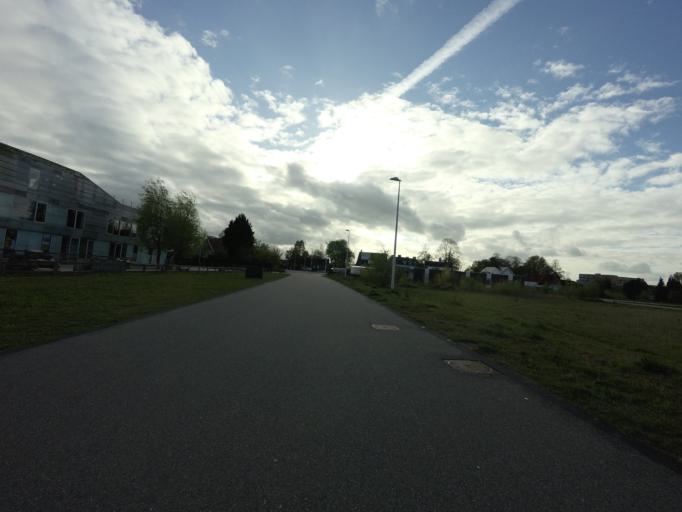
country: NL
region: Utrecht
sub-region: Stichtse Vecht
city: Maarssen
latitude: 52.0957
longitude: 5.0477
